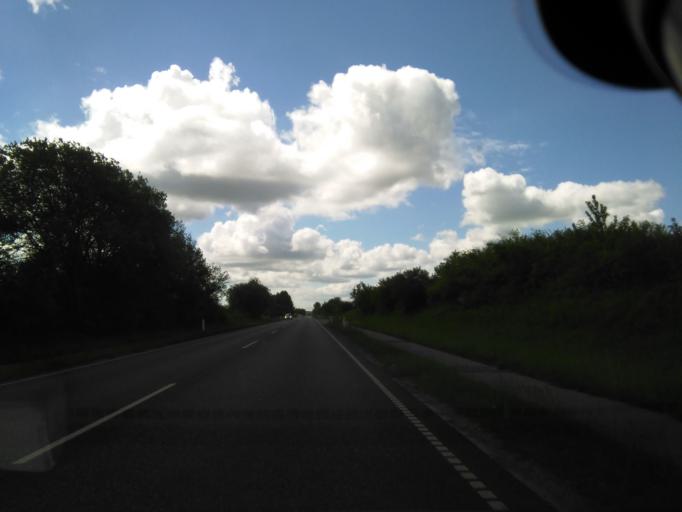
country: DK
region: Central Jutland
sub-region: Arhus Kommune
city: Malling
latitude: 56.0112
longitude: 10.1735
